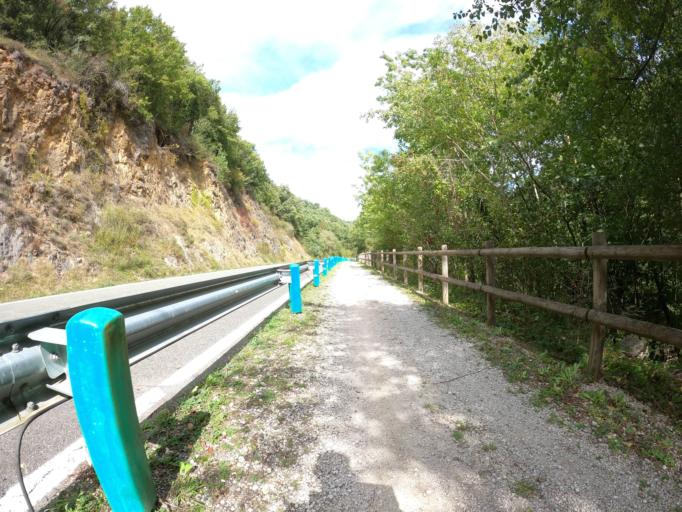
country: ES
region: Navarre
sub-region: Provincia de Navarra
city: Irurtzun
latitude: 42.9478
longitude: -1.8284
